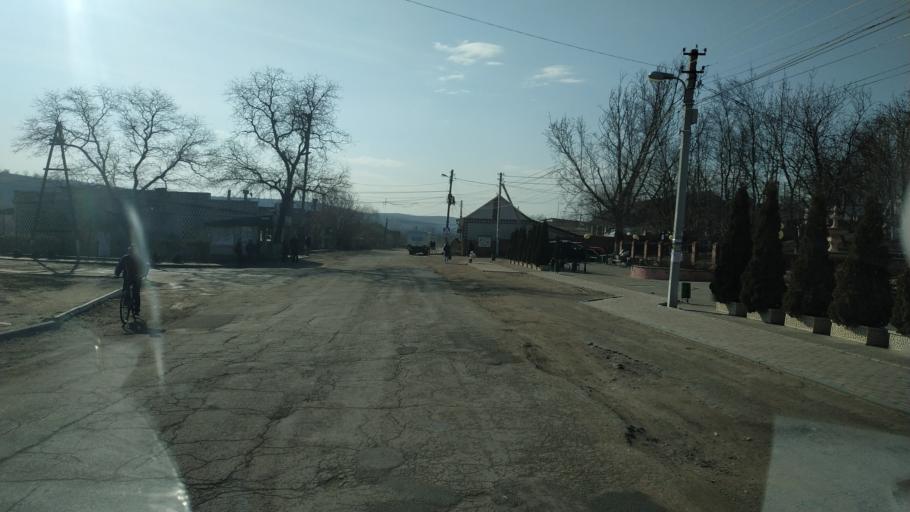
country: MD
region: Chisinau
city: Singera
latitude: 46.8234
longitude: 29.0369
